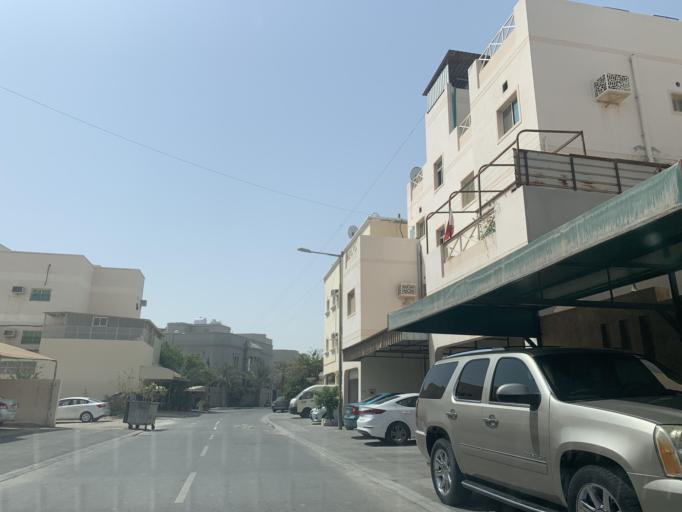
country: BH
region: Northern
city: Madinat `Isa
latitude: 26.1879
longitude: 50.5434
